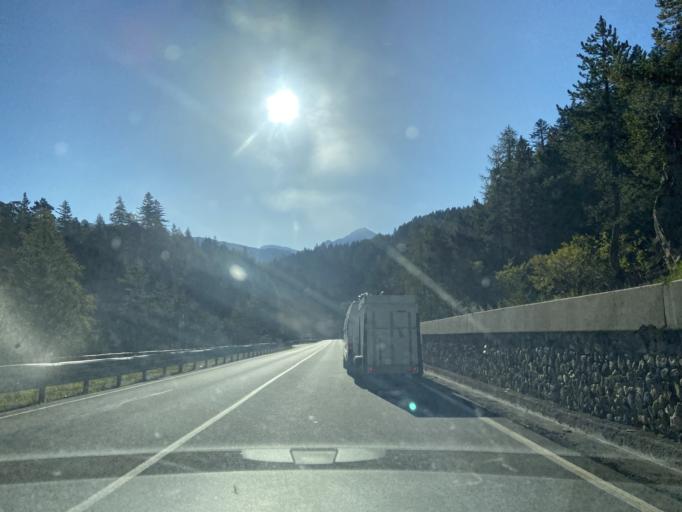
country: IT
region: Piedmont
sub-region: Provincia di Torino
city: Cesana Torinese
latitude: 44.9471
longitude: 6.7736
